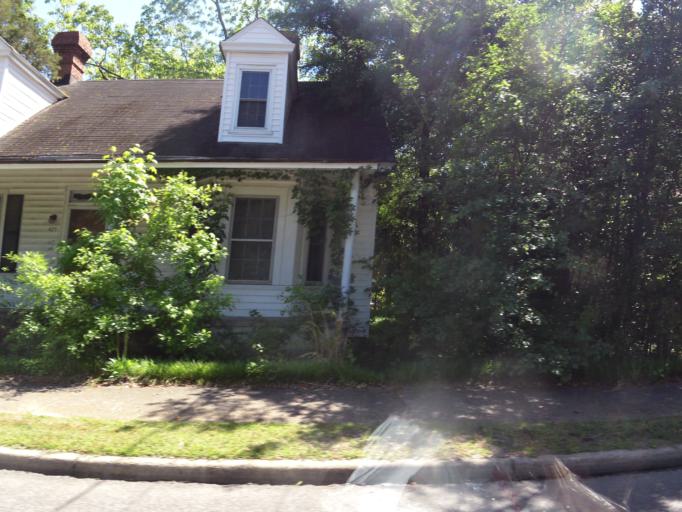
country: US
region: South Carolina
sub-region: Aiken County
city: Aiken
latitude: 33.5588
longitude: -81.7143
